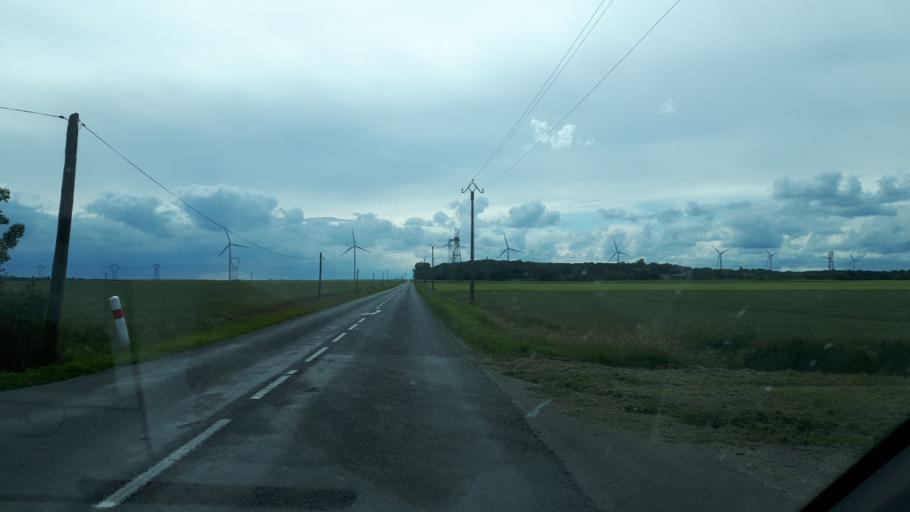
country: FR
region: Centre
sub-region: Departement du Cher
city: Marmagne
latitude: 47.0809
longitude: 2.2616
